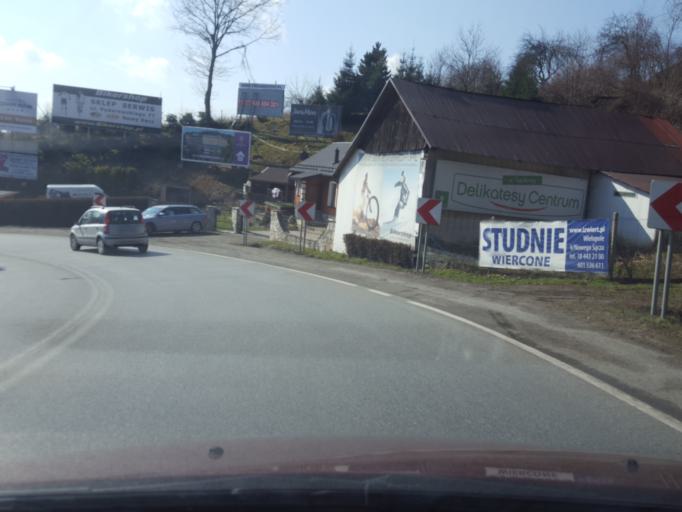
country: PL
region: Lesser Poland Voivodeship
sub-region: Powiat nowosadecki
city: Lososina Dolna
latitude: 49.7222
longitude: 20.6407
